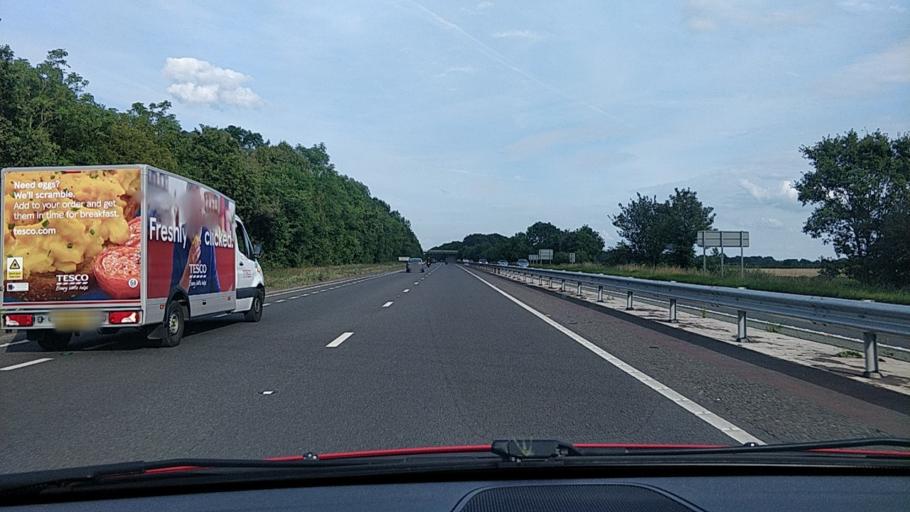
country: GB
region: Wales
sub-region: Wrexham
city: Rossett
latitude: 53.1625
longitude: -2.9648
